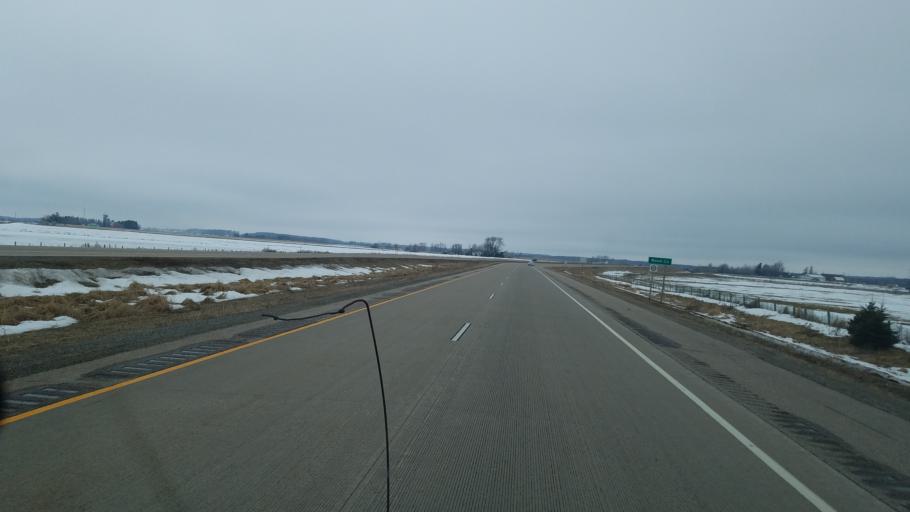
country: US
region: Wisconsin
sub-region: Marathon County
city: Mosinee
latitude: 44.6132
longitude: -89.8462
